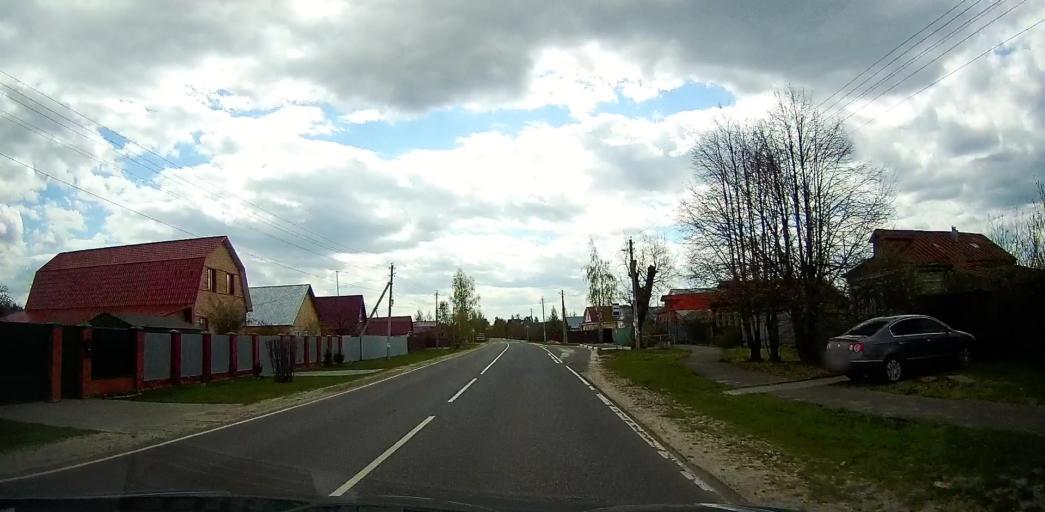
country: RU
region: Moskovskaya
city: Davydovo
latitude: 55.6651
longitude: 38.7594
